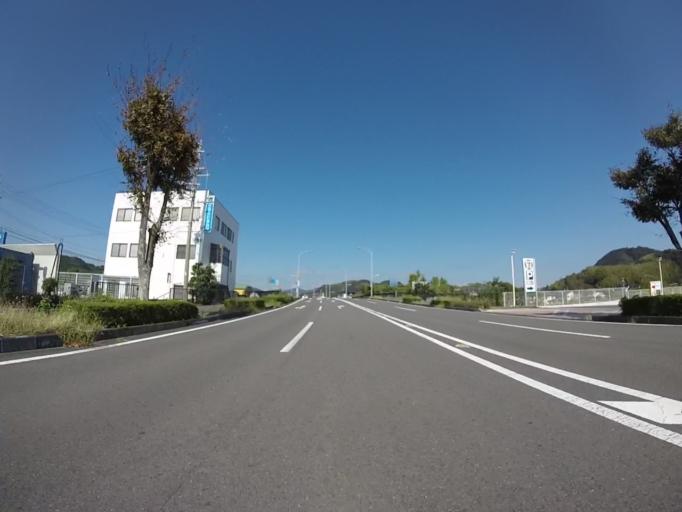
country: JP
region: Shizuoka
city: Fujieda
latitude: 34.8842
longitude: 138.2635
